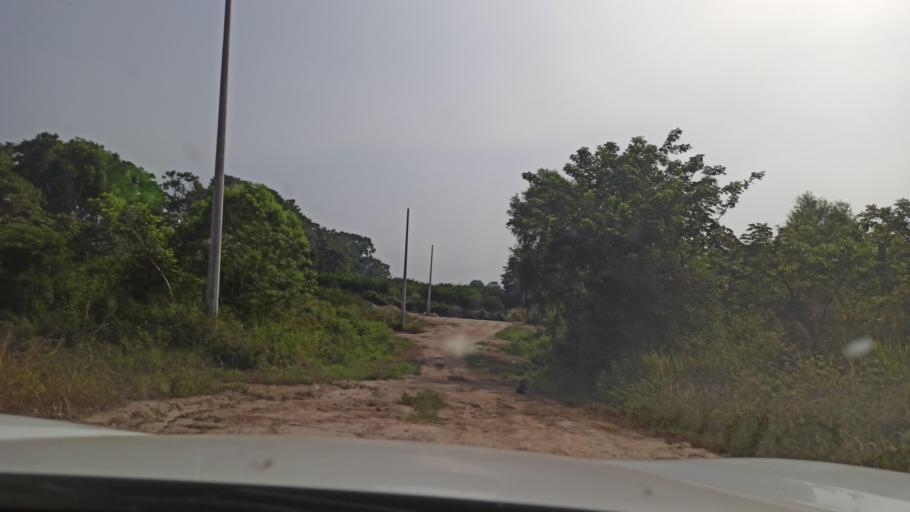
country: MX
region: Veracruz
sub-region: Martinez de la Torre
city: El Progreso
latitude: 20.1492
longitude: -97.0673
